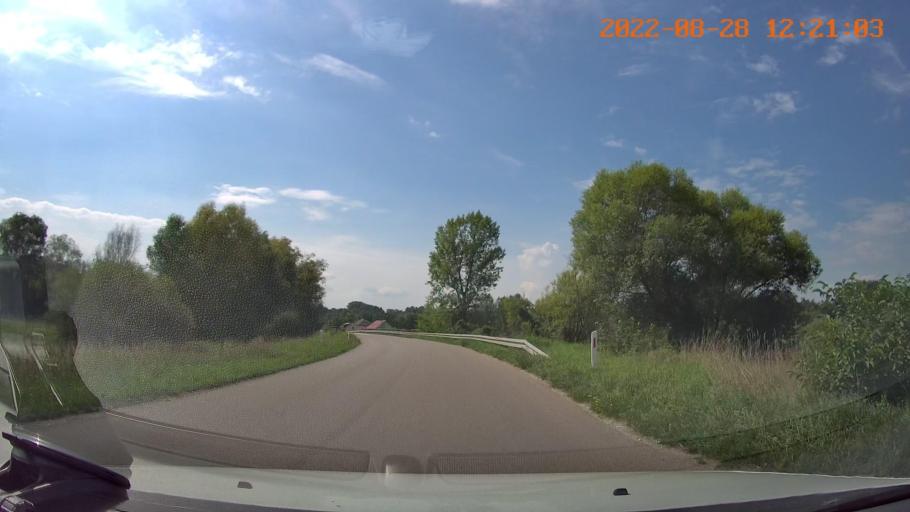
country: PL
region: Swietokrzyskie
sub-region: Powiat pinczowski
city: Zlota
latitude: 50.4261
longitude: 20.5608
